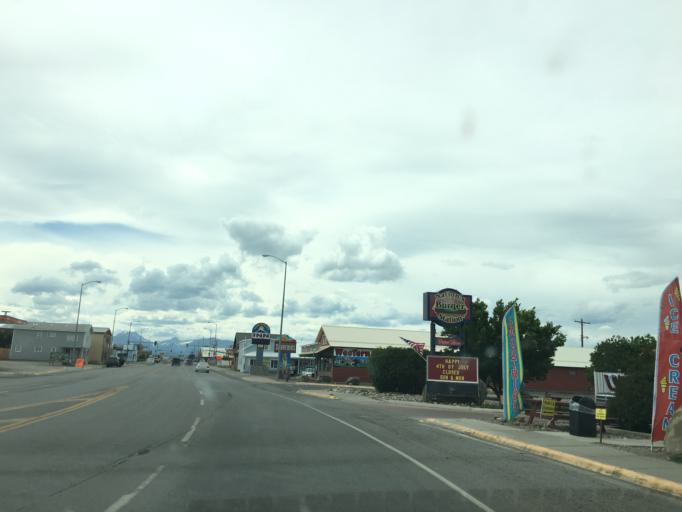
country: US
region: Montana
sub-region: Glacier County
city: Browning
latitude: 48.5559
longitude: -113.0107
